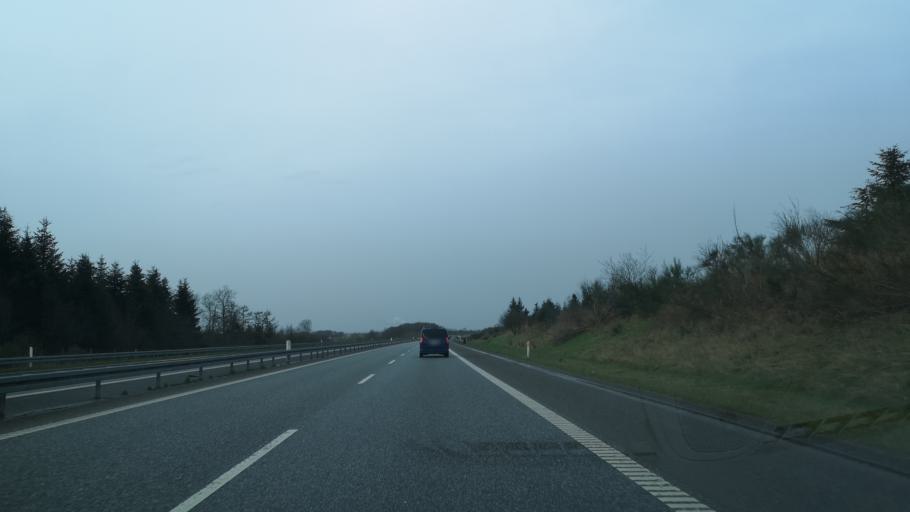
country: DK
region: Central Jutland
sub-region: Herning Kommune
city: Lind
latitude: 56.0827
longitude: 8.9984
